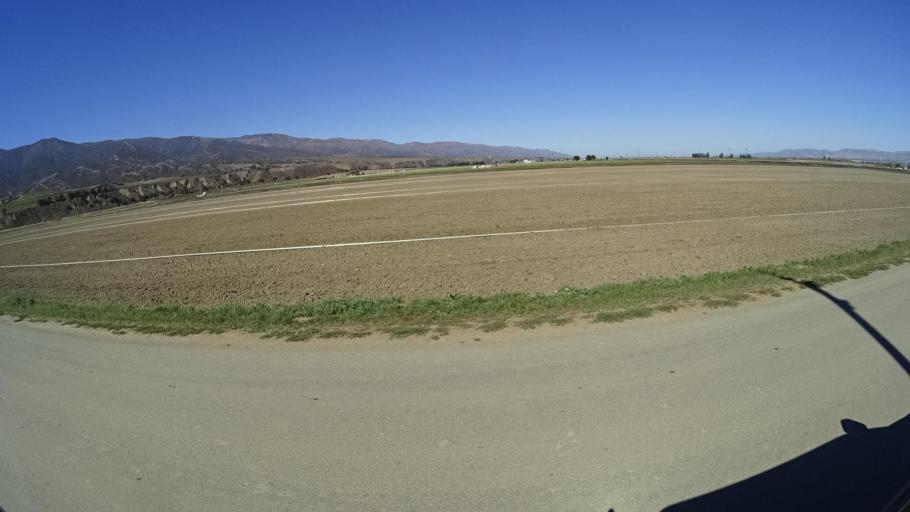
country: US
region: California
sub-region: Monterey County
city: Soledad
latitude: 36.4020
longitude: -121.3607
